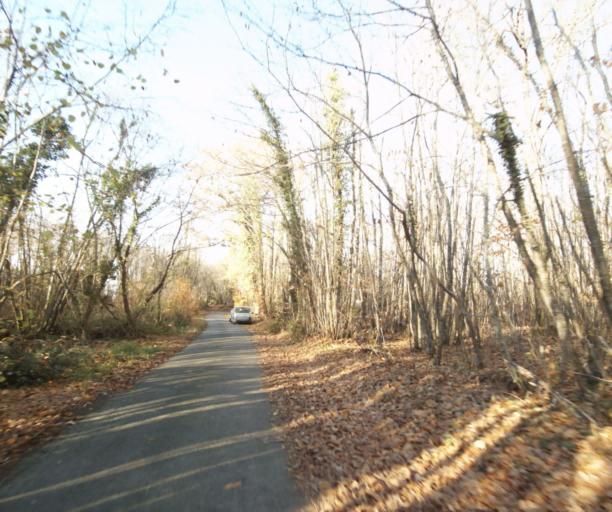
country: FR
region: Poitou-Charentes
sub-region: Departement de la Charente-Maritime
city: Cherac
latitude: 45.7254
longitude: -0.4689
